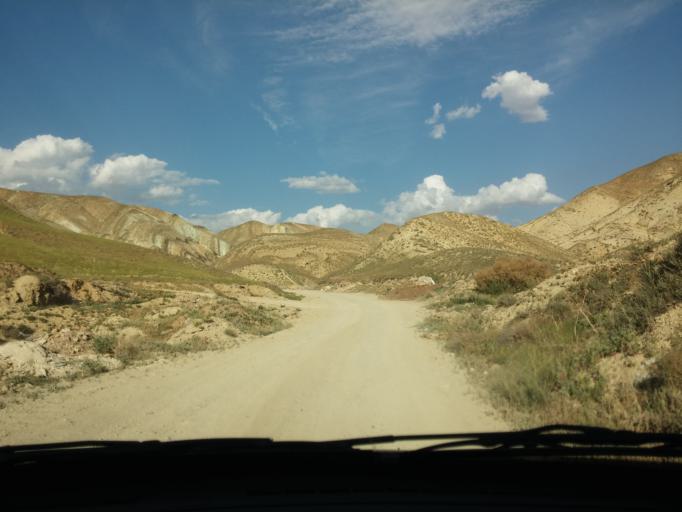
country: IR
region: Tehran
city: Damavand
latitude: 35.5380
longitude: 52.1792
